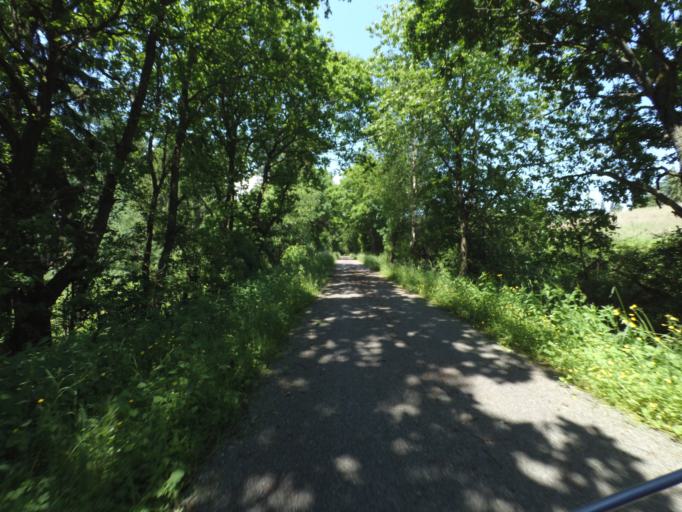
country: DE
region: Rheinland-Pfalz
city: Leiningen
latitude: 50.1238
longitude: 7.5682
